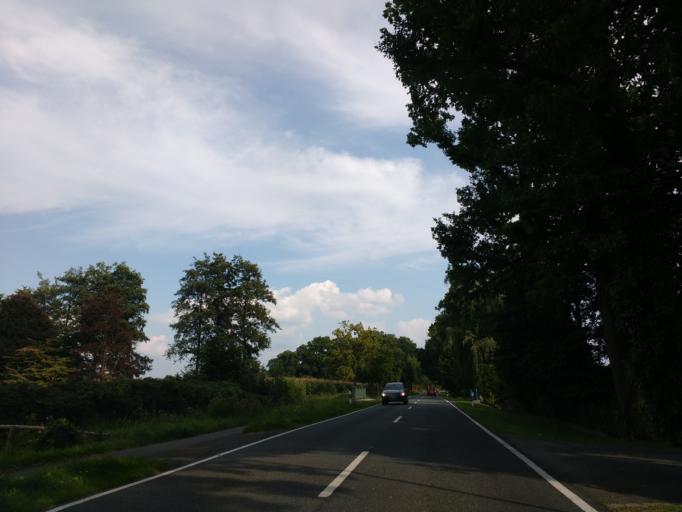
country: DE
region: North Rhine-Westphalia
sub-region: Regierungsbezirk Detmold
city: Hovelhof
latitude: 51.7698
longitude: 8.6430
